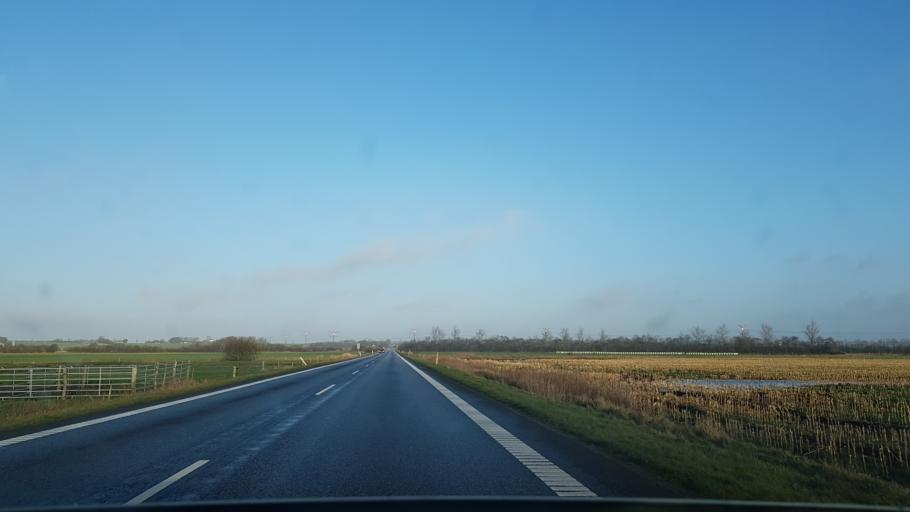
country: DK
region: South Denmark
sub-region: Tonder Kommune
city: Toftlund
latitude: 55.2375
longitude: 9.1275
